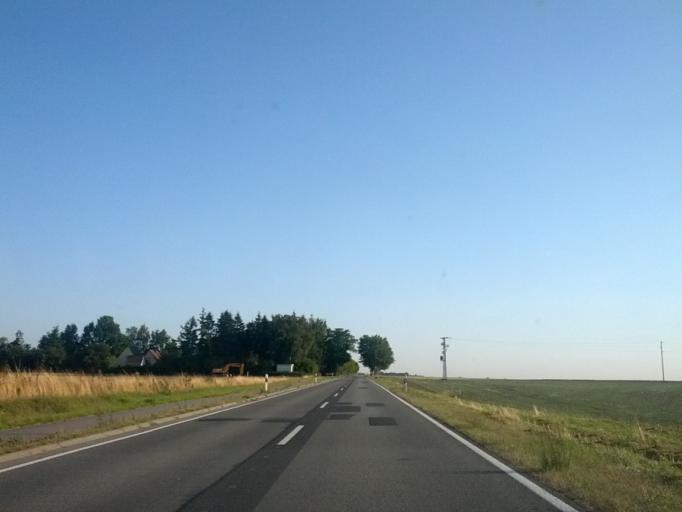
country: DE
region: Mecklenburg-Vorpommern
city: Brandshagen
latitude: 54.1712
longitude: 13.1800
